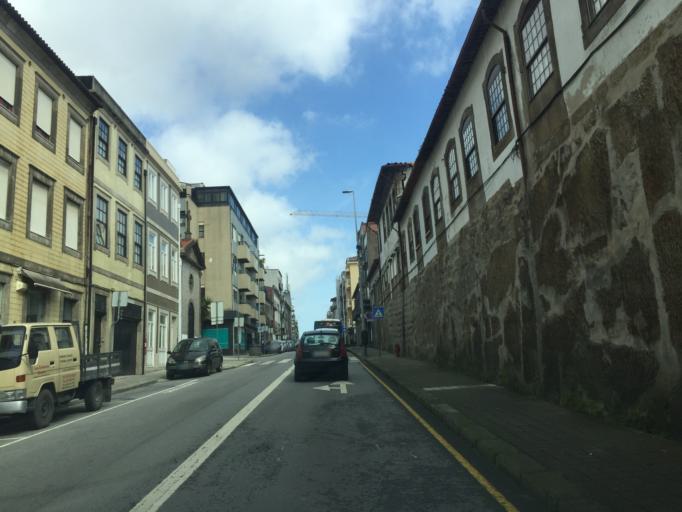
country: PT
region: Porto
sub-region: Porto
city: Porto
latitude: 41.1582
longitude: -8.6122
